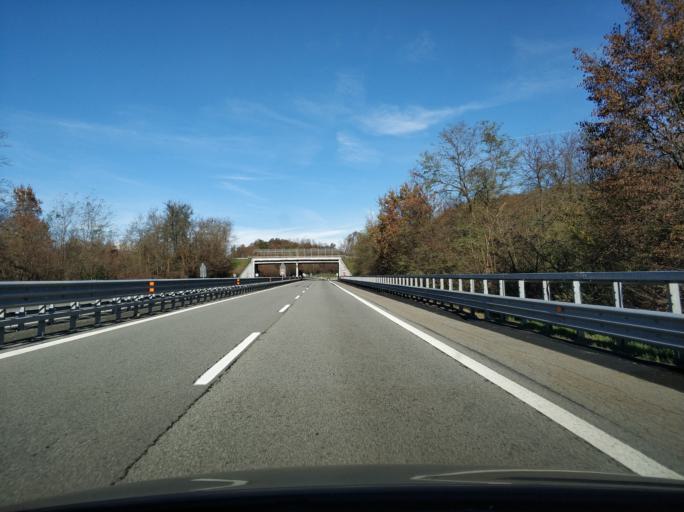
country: IT
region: Piedmont
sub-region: Provincia di Torino
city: Montalenghe
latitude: 45.3519
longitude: 7.8316
